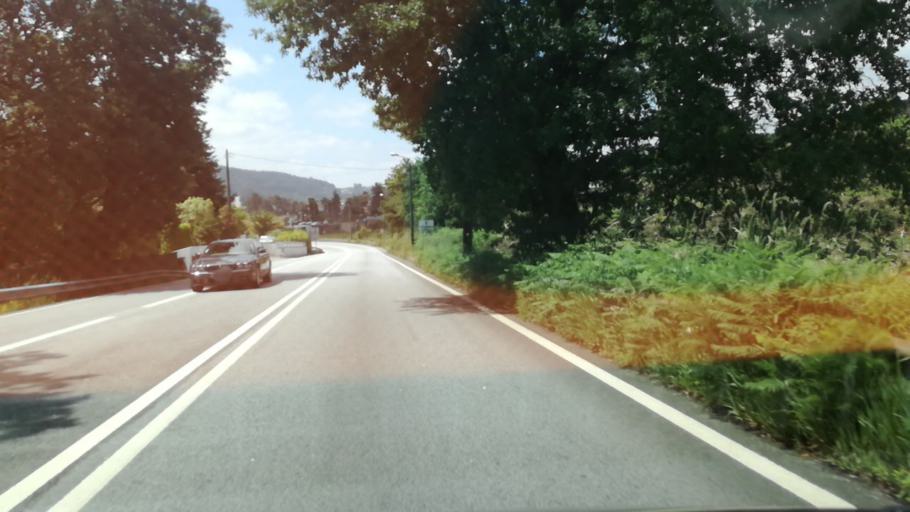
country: PT
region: Braga
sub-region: Braga
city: Braga
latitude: 41.5221
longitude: -8.4495
